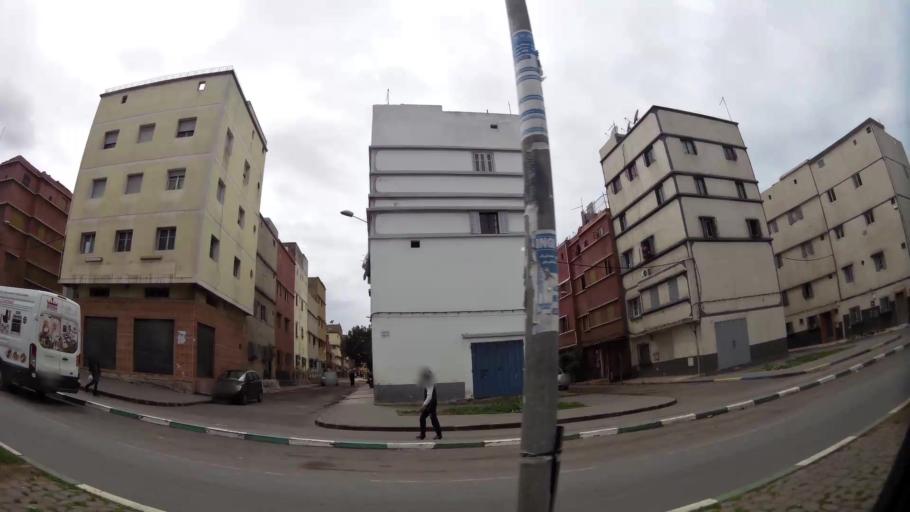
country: MA
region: Grand Casablanca
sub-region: Mediouna
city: Tit Mellil
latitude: 33.6128
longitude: -7.5019
